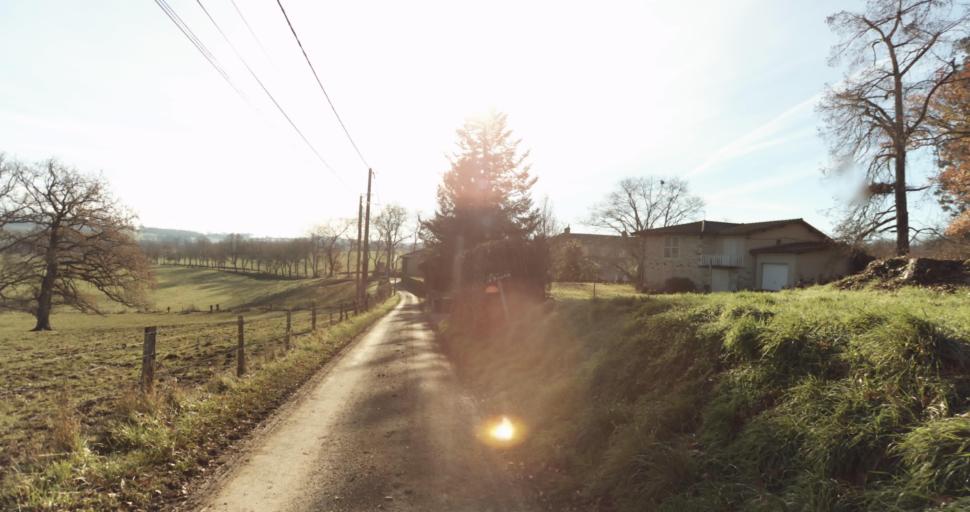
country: FR
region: Limousin
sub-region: Departement de la Haute-Vienne
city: Saint-Priest-sous-Aixe
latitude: 45.7891
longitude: 1.1024
